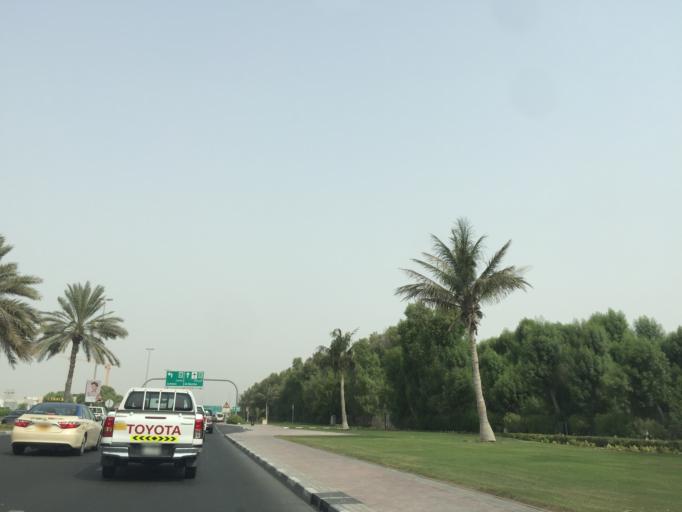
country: AE
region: Dubai
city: Dubai
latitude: 25.1298
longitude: 55.1923
